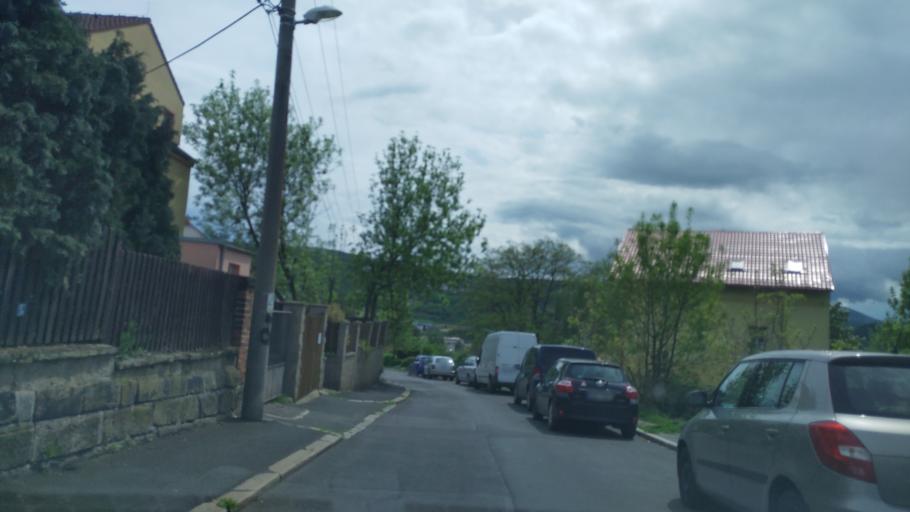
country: CZ
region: Ustecky
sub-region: Okres Usti nad Labem
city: Usti nad Labem
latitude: 50.6625
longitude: 14.0123
